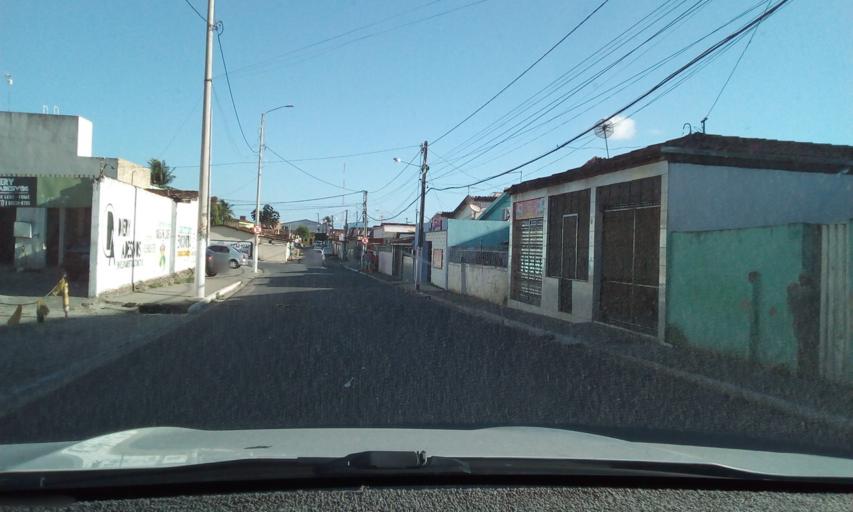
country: BR
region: Paraiba
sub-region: Bayeux
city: Bayeux
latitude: -7.1257
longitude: -34.9248
